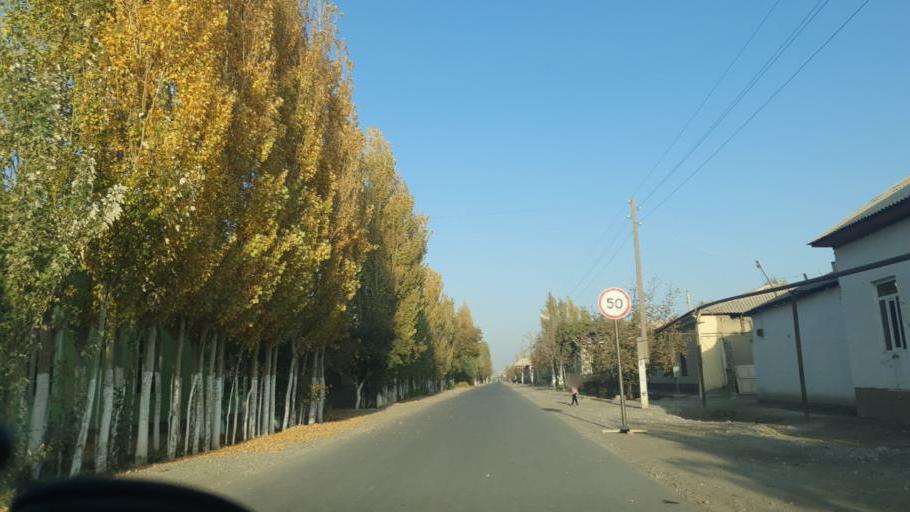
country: UZ
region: Fergana
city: Beshariq
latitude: 40.4641
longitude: 70.5506
